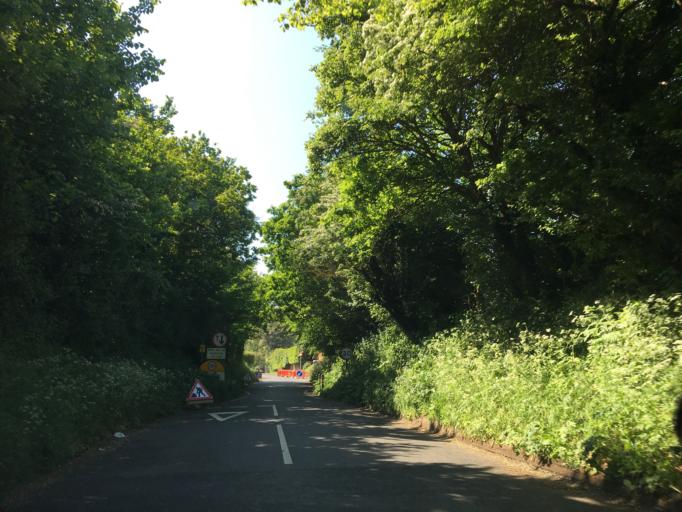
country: GB
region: England
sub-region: Isle of Wight
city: Newchurch
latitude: 50.6719
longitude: -1.2108
